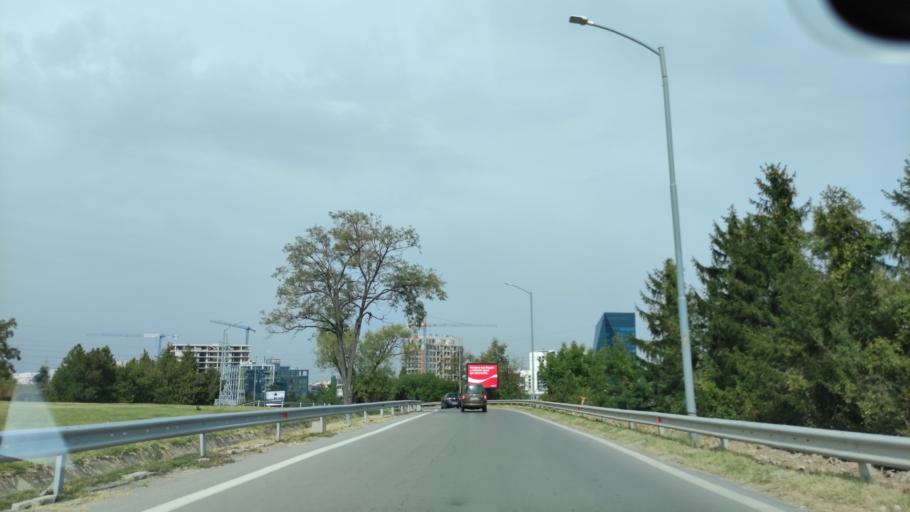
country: BG
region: Sofia-Capital
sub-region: Stolichna Obshtina
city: Sofia
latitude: 42.6528
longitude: 23.2866
